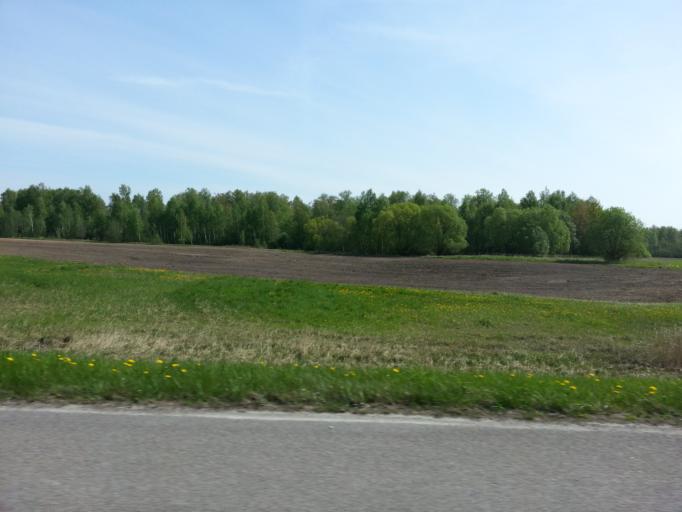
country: LT
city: Ramygala
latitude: 55.5860
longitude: 24.4572
